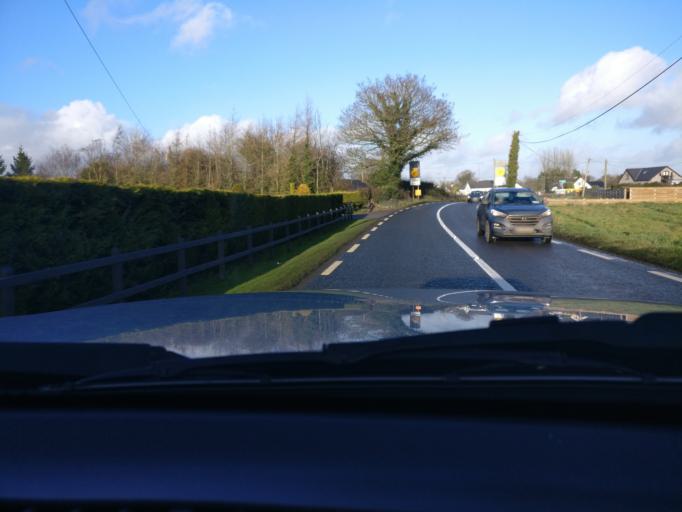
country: IE
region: Leinster
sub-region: An Iarmhi
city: Rathwire
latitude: 53.5691
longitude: -7.1896
